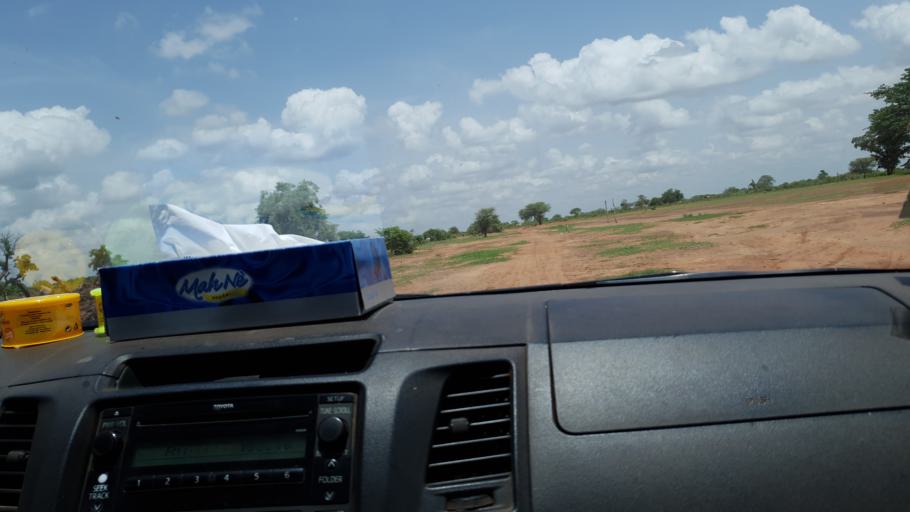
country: ML
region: Koulikoro
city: Banamba
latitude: 13.3790
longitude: -7.2046
